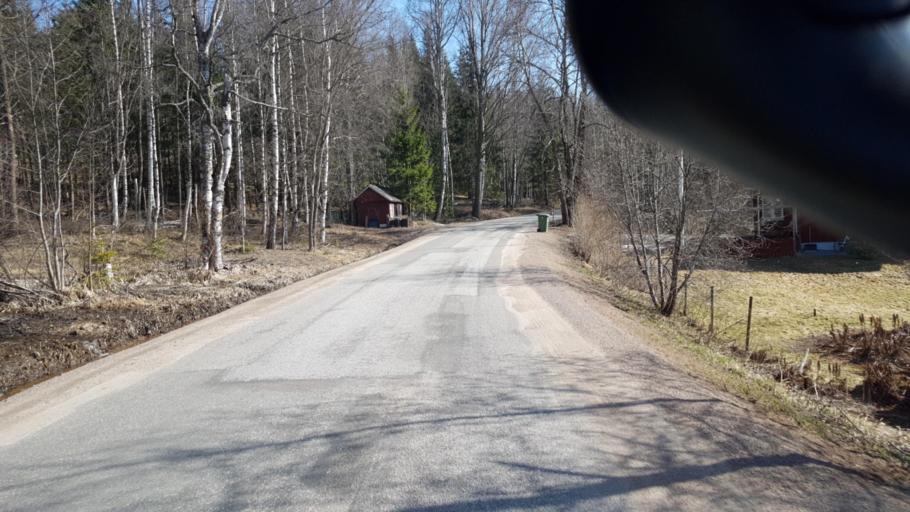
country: SE
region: Vaermland
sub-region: Arvika Kommun
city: Arvika
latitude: 59.6527
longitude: 12.8077
